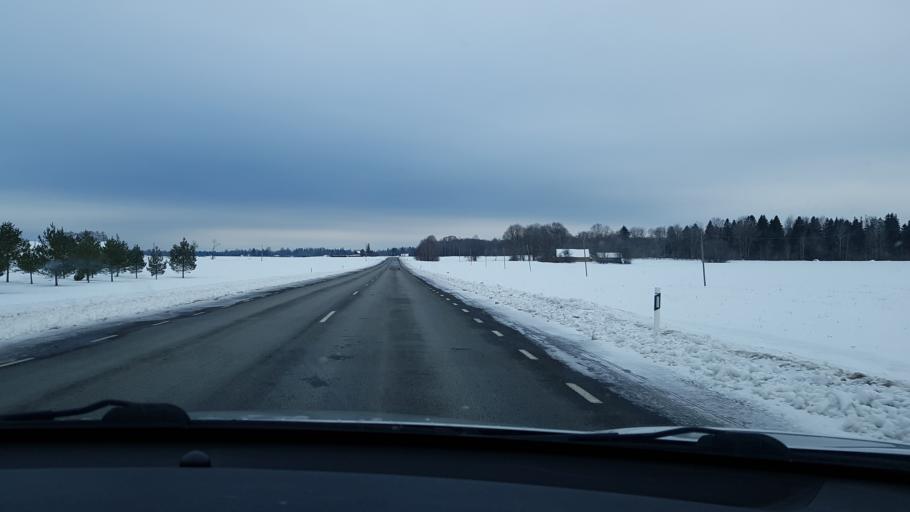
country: EE
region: Jaervamaa
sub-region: Paide linn
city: Paide
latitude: 58.8868
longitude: 25.7104
